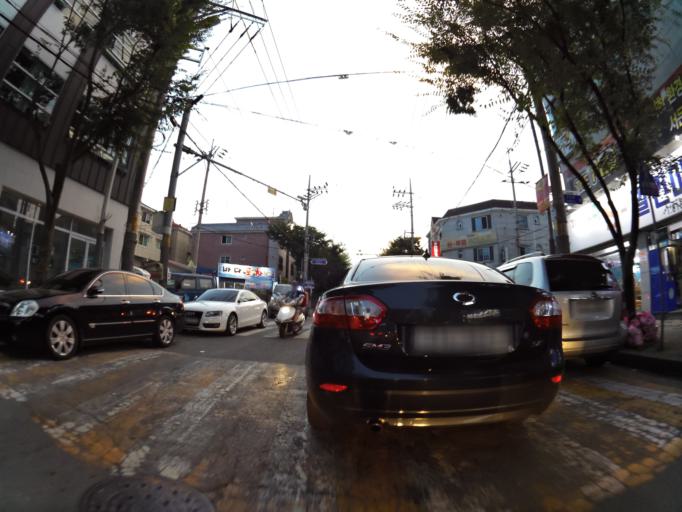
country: KR
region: Gyeongsangbuk-do
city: Gyeongsan-si
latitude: 35.8427
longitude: 128.7499
